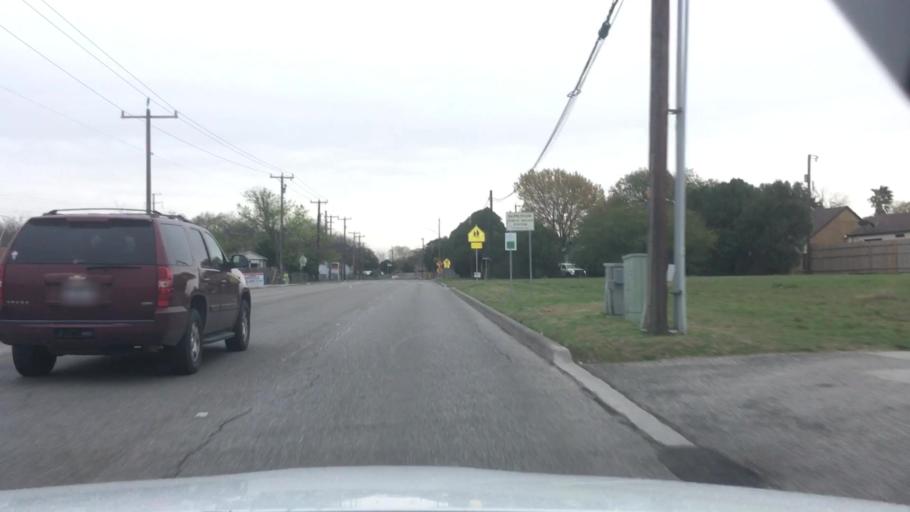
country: US
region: Texas
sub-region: Bexar County
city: Windcrest
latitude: 29.5238
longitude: -98.3888
